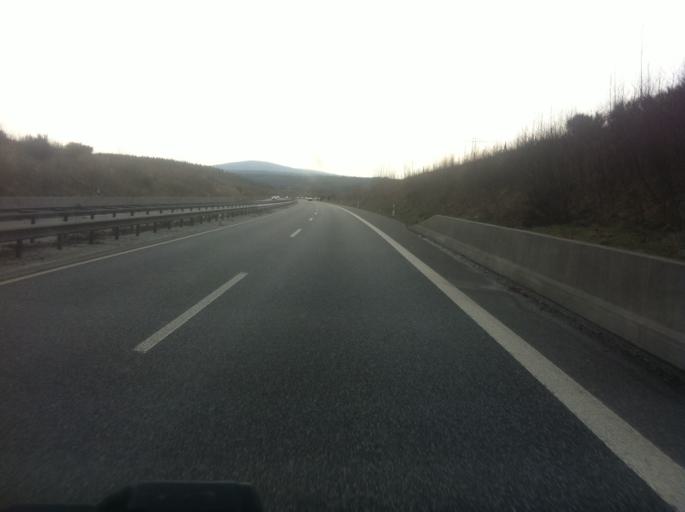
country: DE
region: Rheinland-Pfalz
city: Kirchberg
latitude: 49.9486
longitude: 7.3911
